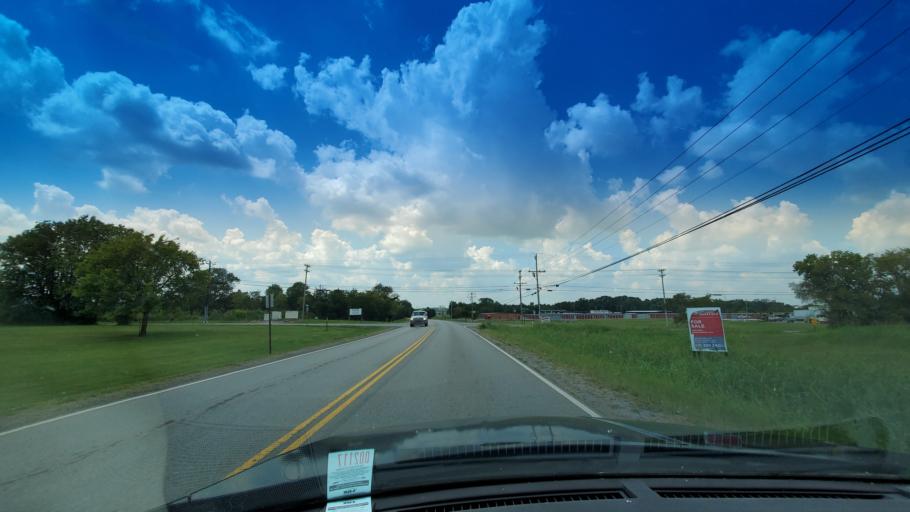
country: US
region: Tennessee
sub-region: Wilson County
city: Lebanon
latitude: 36.1731
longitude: -86.2929
